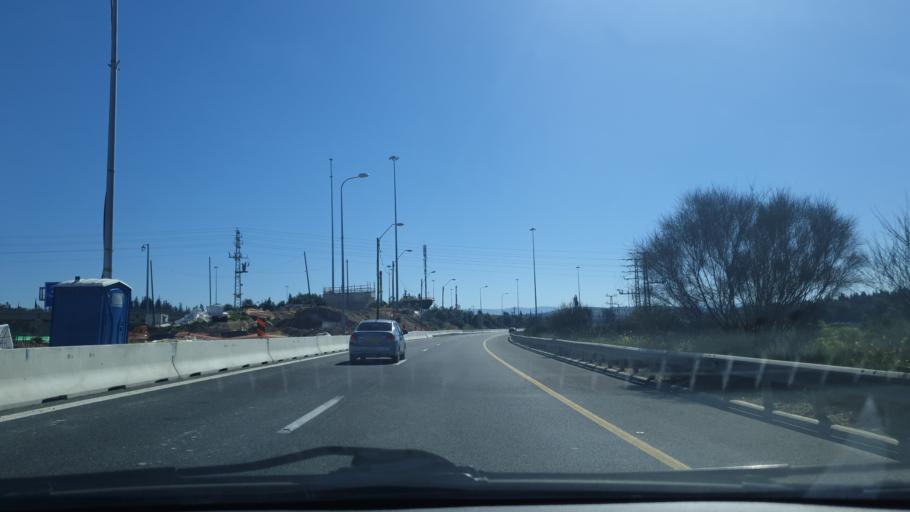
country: IL
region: Central District
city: Lod
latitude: 31.9005
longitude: 34.9331
